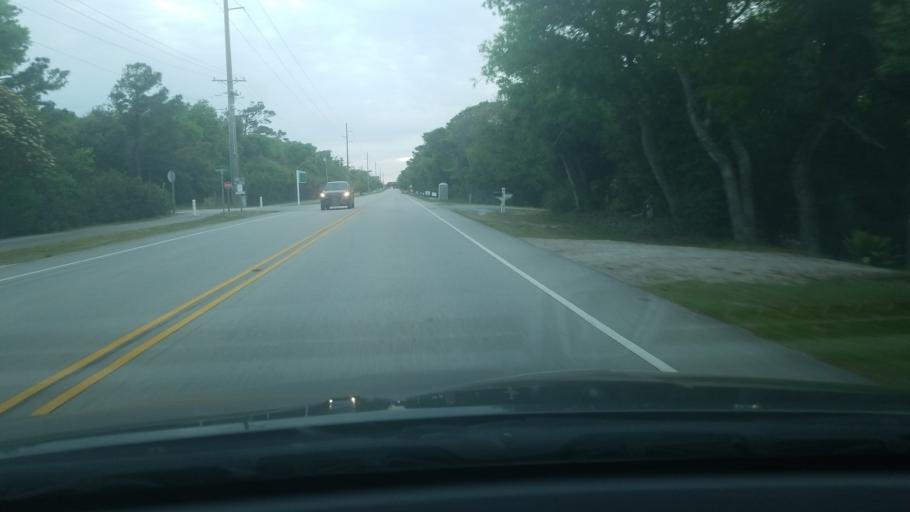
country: US
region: North Carolina
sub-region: Carteret County
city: Cape Carteret
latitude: 34.6690
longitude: -77.0129
